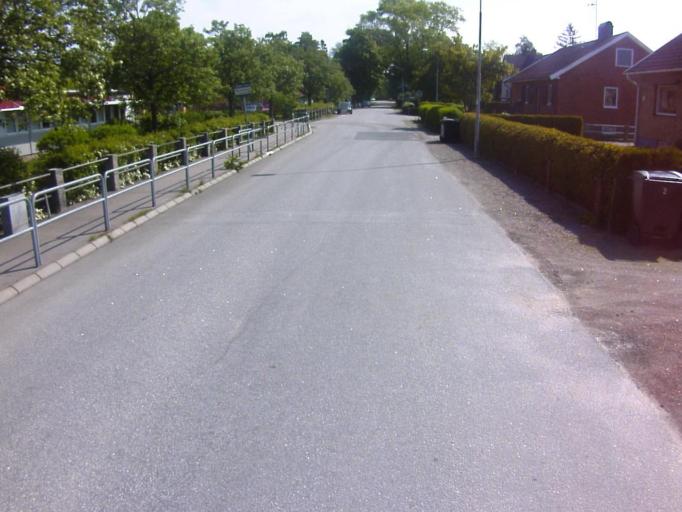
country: SE
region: Blekinge
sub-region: Solvesborgs Kommun
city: Soelvesborg
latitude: 56.0478
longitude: 14.6762
